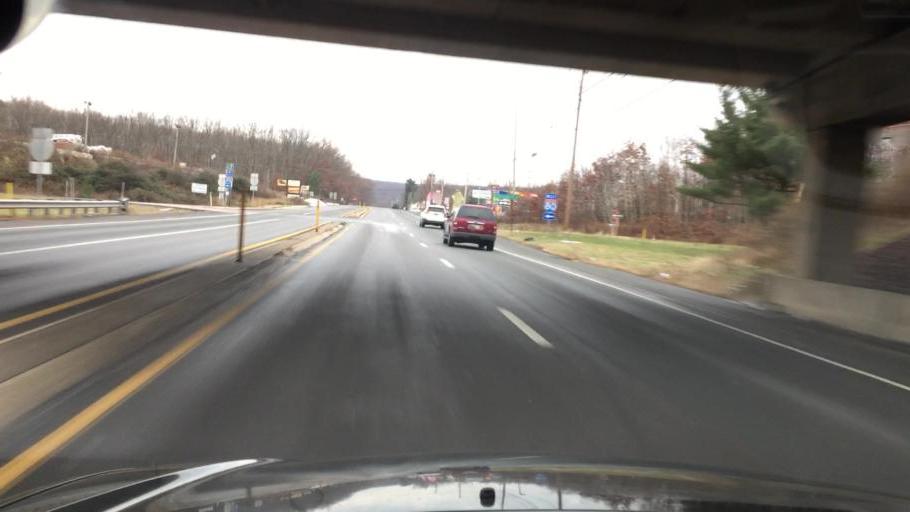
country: US
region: Pennsylvania
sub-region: Luzerne County
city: Freeland
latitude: 41.0537
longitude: -75.9598
